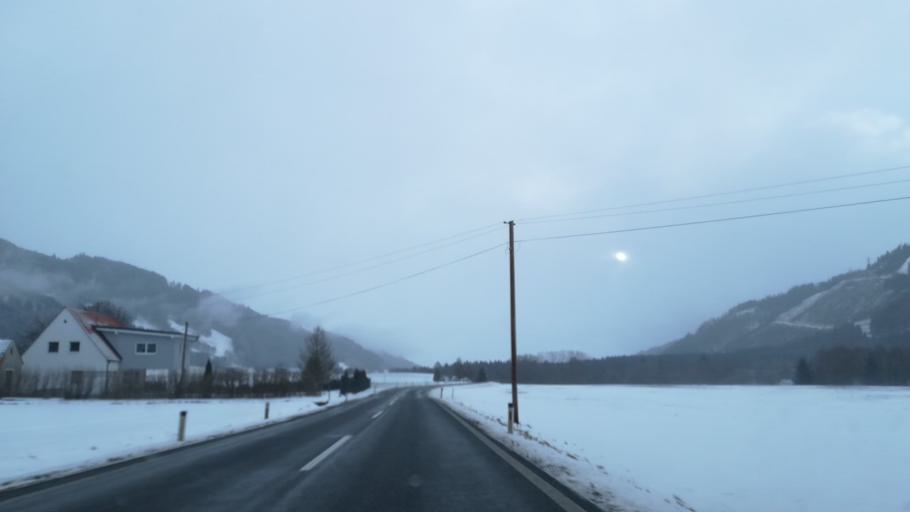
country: AT
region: Styria
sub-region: Politischer Bezirk Murtal
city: Poels
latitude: 47.2225
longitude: 14.5974
